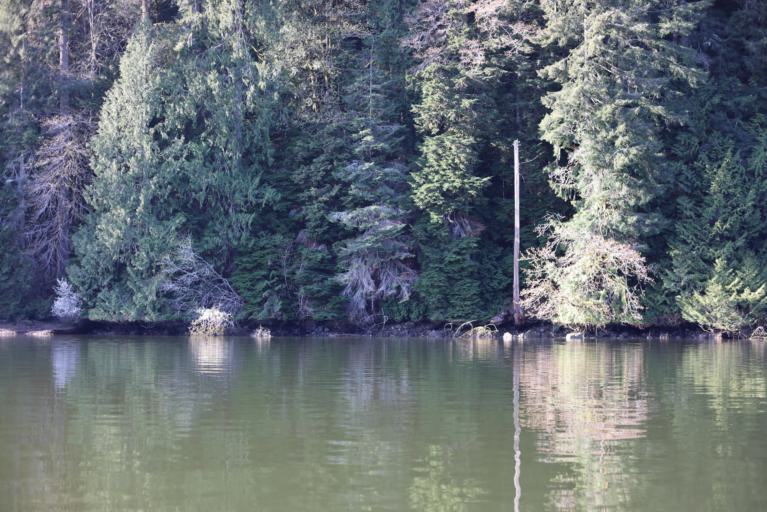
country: CA
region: British Columbia
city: Langford
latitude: 48.5594
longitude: -123.4725
